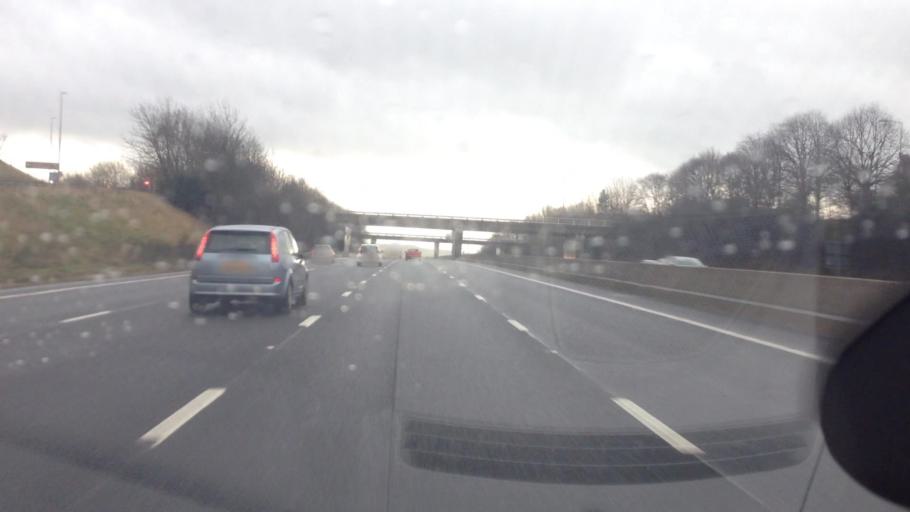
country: GB
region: England
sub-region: City and Borough of Wakefield
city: Ossett
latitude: 53.6856
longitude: -1.5555
